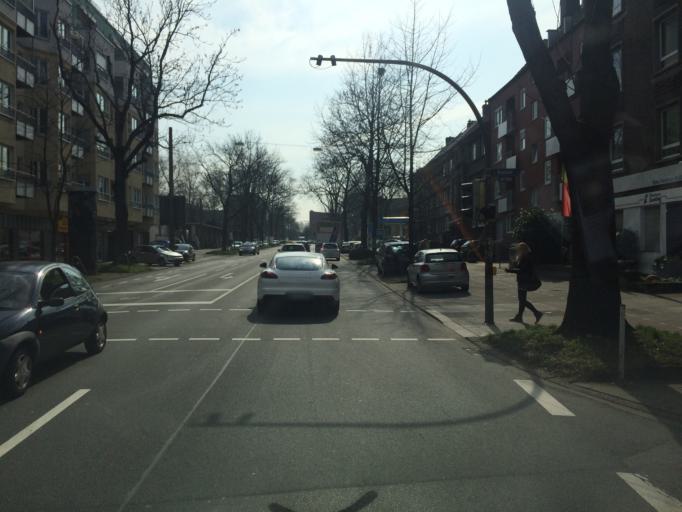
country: DE
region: North Rhine-Westphalia
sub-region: Regierungsbezirk Arnsberg
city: Dortmund
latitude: 51.5025
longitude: 7.4519
